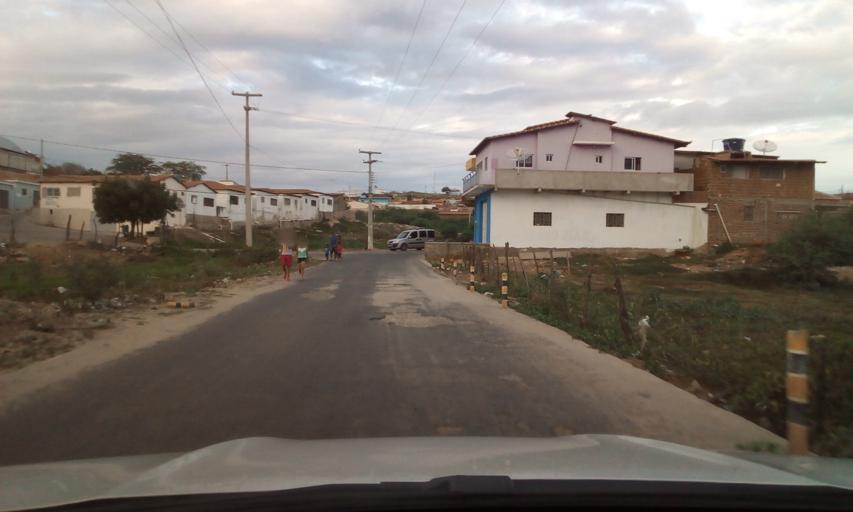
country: BR
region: Paraiba
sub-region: Picui
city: Picui
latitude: -6.5105
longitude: -36.3439
